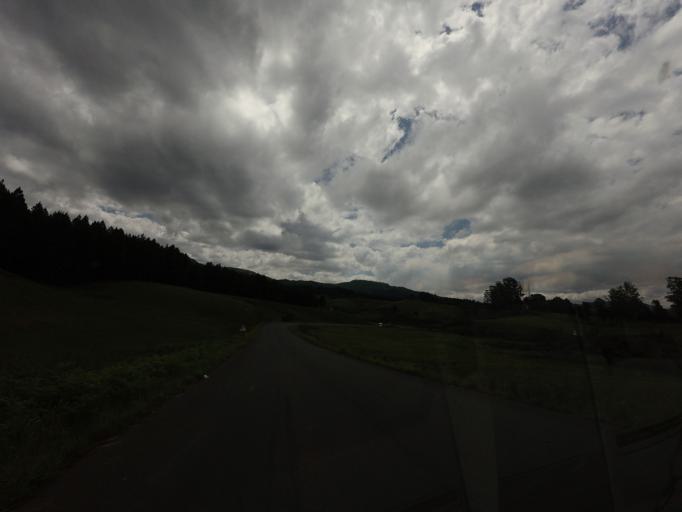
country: ZA
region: Mpumalanga
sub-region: Ehlanzeni District
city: Graksop
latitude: -24.9976
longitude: 30.8139
